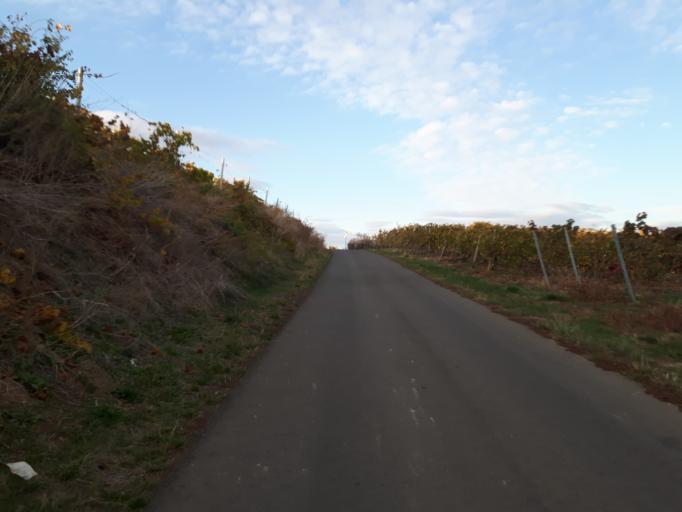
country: DE
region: Rheinland-Pfalz
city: Molsheim
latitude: 49.6292
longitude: 8.1795
